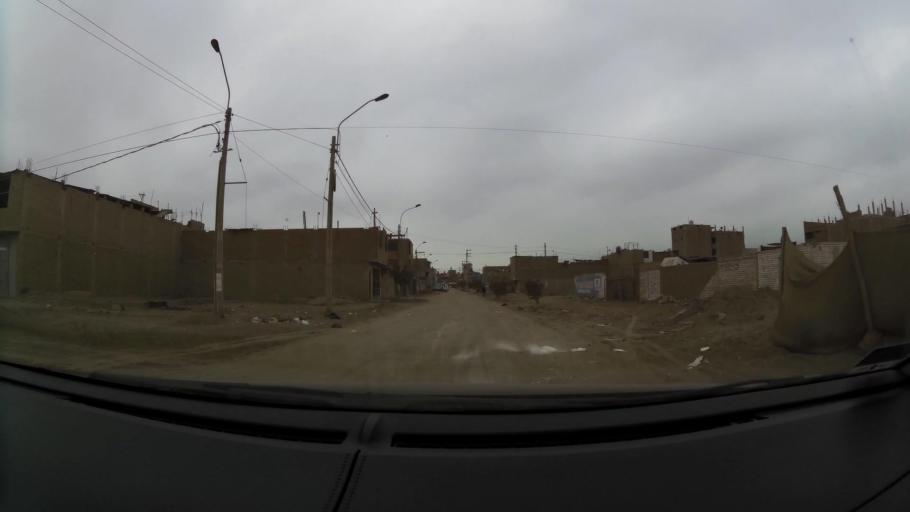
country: PE
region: Lima
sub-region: Lima
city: Independencia
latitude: -11.9664
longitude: -77.0945
